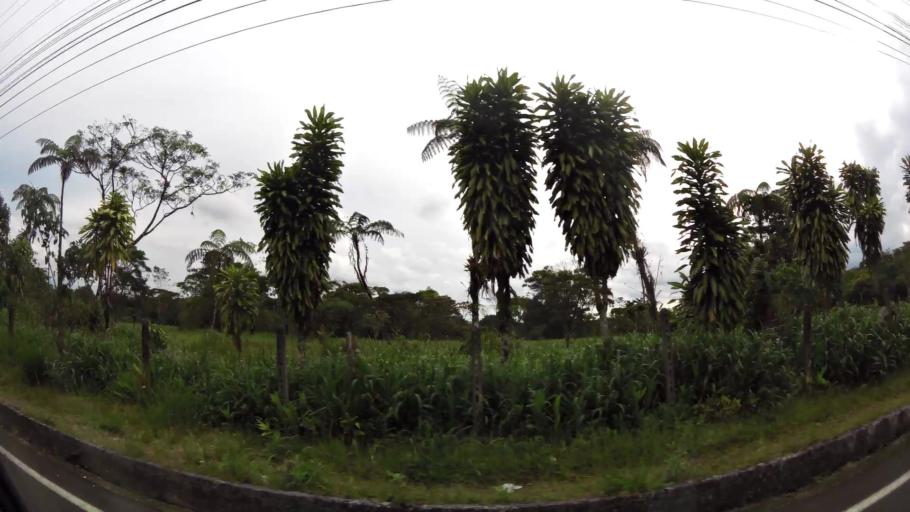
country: EC
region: Pastaza
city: Puyo
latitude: -1.5073
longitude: -78.0323
